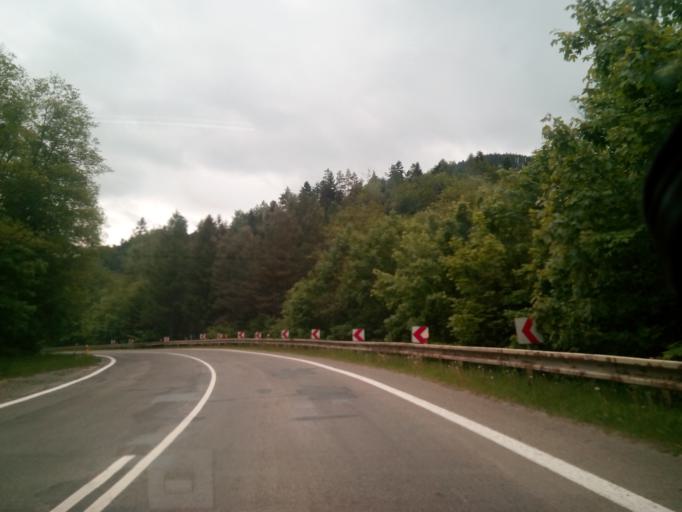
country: SK
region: Kosicky
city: Krompachy
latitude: 48.9993
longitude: 20.8814
